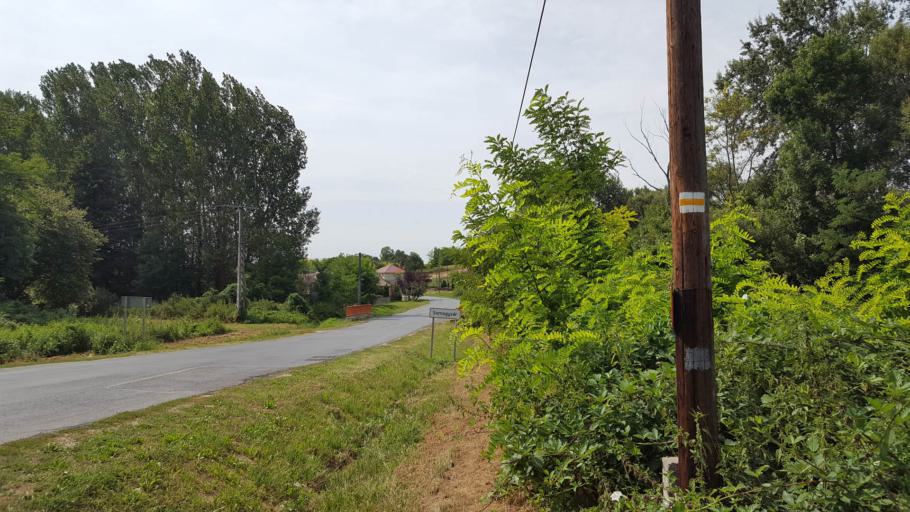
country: HU
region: Somogy
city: Somogyvar
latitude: 46.5831
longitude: 17.6725
